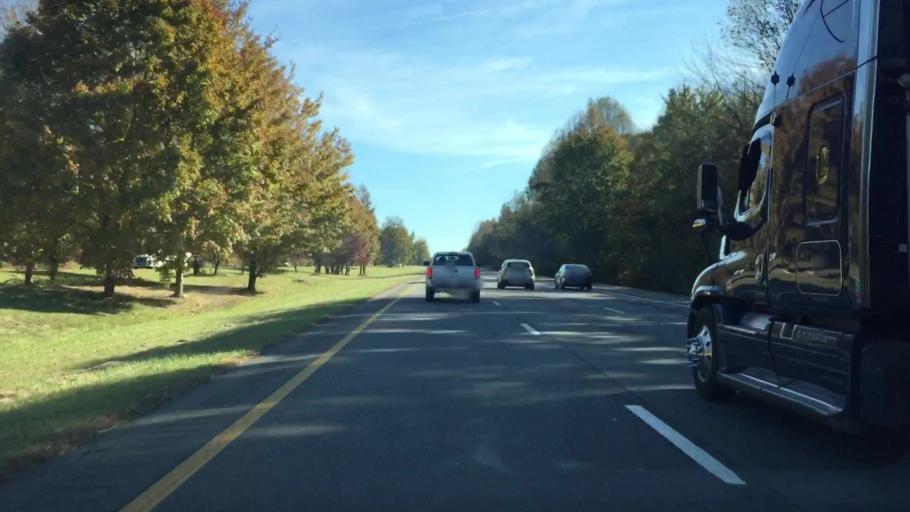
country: US
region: North Carolina
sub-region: Davidson County
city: Lexington
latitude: 35.7768
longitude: -80.2884
